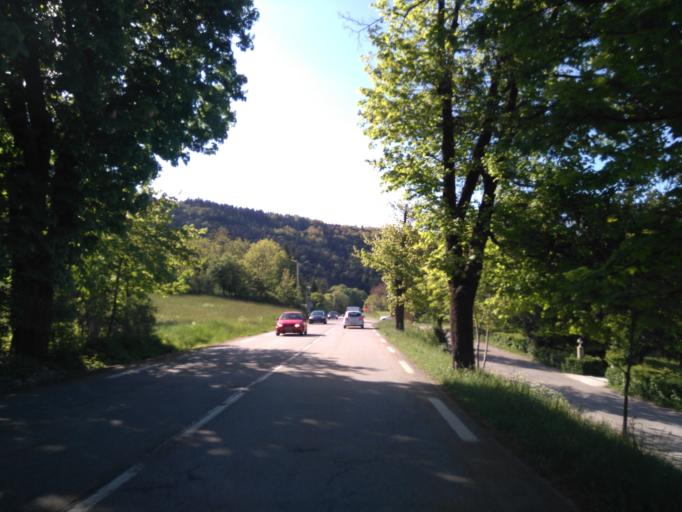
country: FR
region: Rhone-Alpes
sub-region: Departement de l'Isere
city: Mens
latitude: 44.7613
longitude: 5.6626
